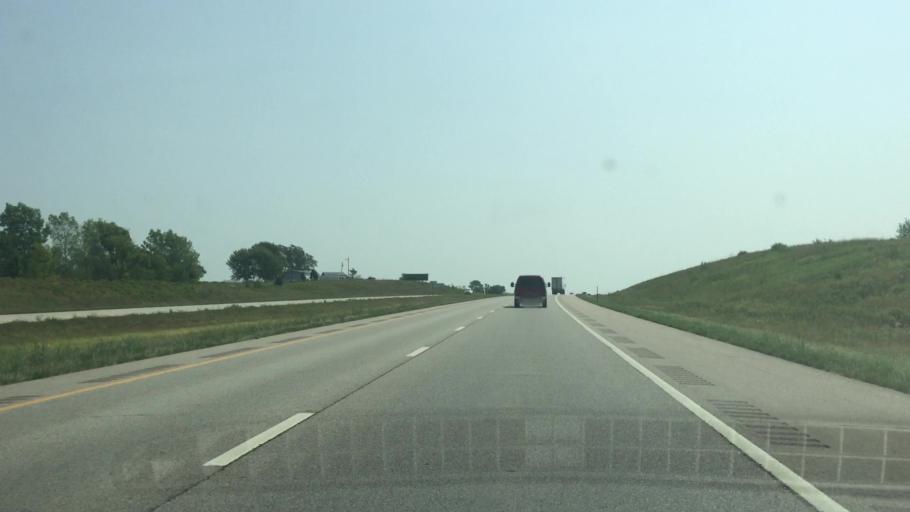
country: US
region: Kansas
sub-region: Lyon County
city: Emporia
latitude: 38.4110
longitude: -96.0785
